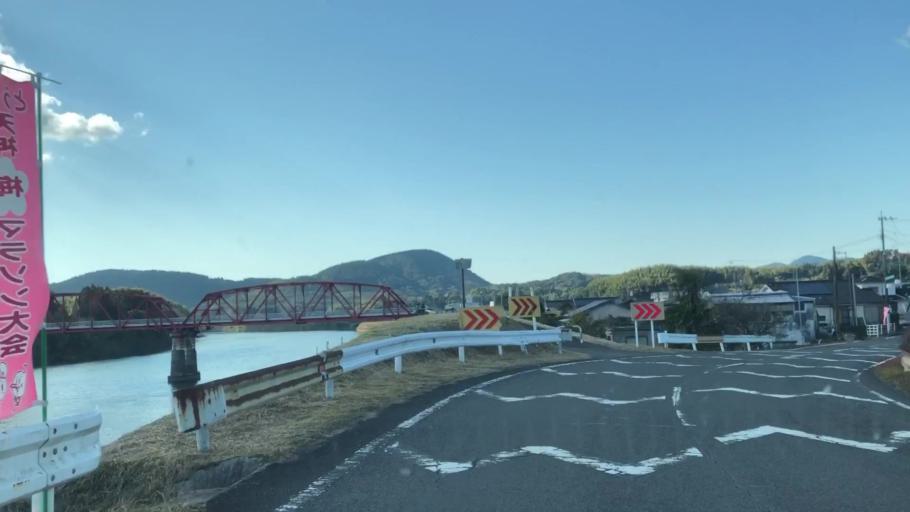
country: JP
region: Kagoshima
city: Satsumasendai
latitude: 31.8618
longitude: 130.3387
